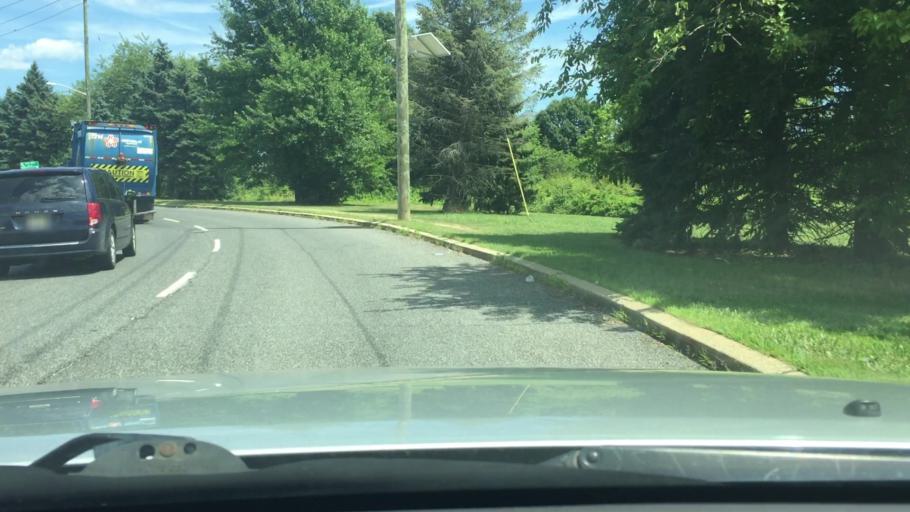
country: US
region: New Jersey
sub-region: Middlesex County
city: South River
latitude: 40.4361
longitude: -74.3956
